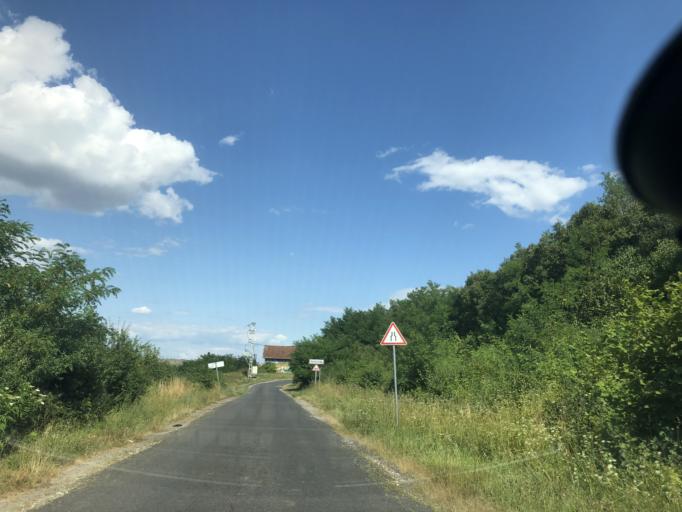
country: HU
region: Borsod-Abauj-Zemplen
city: Szendro
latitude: 48.5454
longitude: 20.8007
